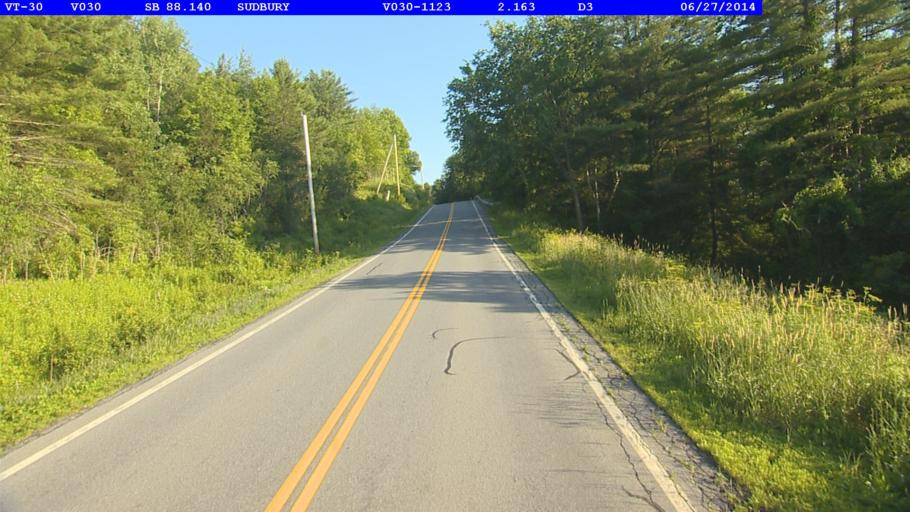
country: US
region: Vermont
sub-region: Rutland County
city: Brandon
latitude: 43.7792
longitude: -73.2036
